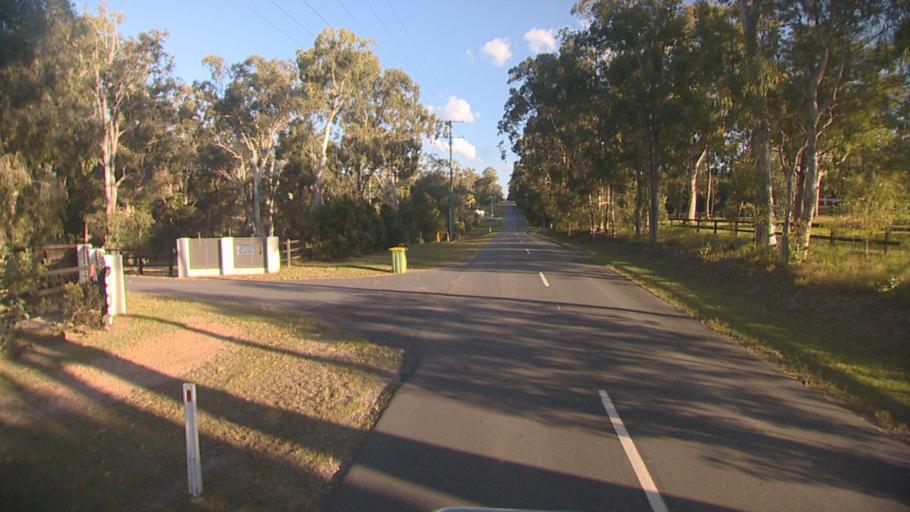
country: AU
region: Queensland
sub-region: Redland
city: Redland Bay
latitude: -27.6751
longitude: 153.2762
